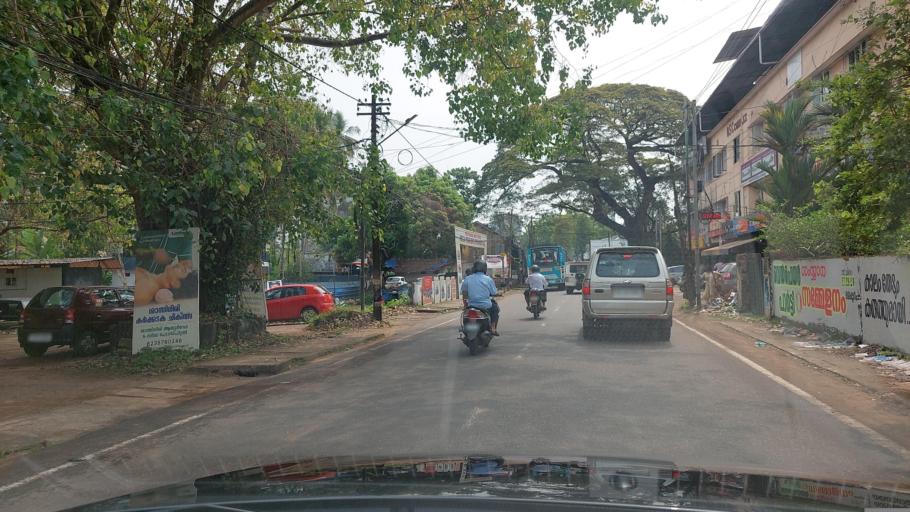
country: IN
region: Kerala
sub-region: Kozhikode
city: Kozhikode
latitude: 11.2692
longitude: 75.7778
